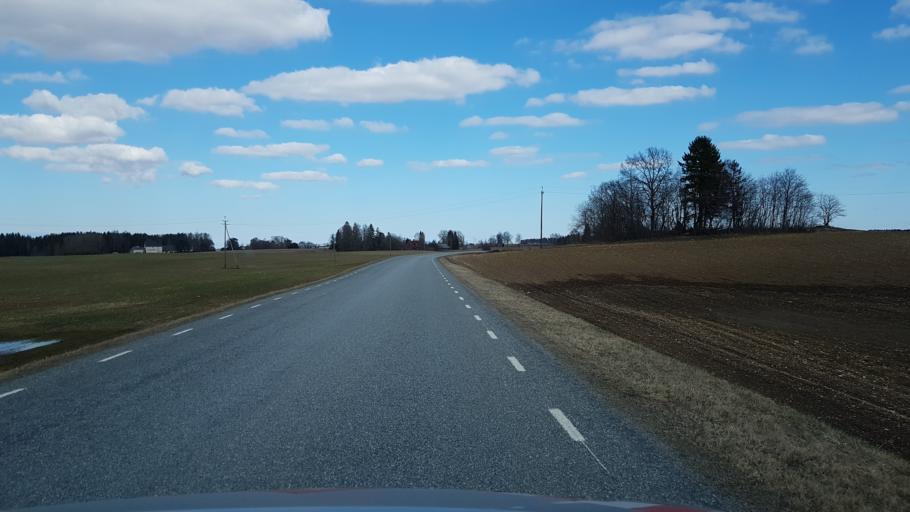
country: EE
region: Laeaene-Virumaa
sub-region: Rakvere linn
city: Rakvere
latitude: 59.2681
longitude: 26.2736
